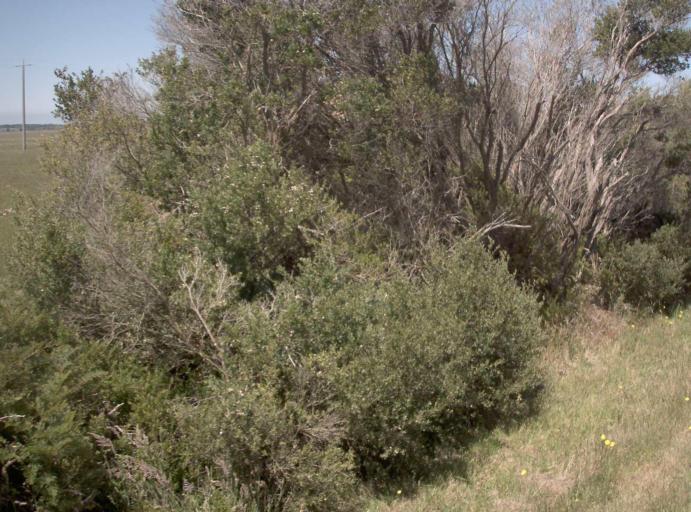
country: AU
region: Victoria
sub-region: Bass Coast
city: North Wonthaggi
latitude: -38.8141
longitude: 146.1033
